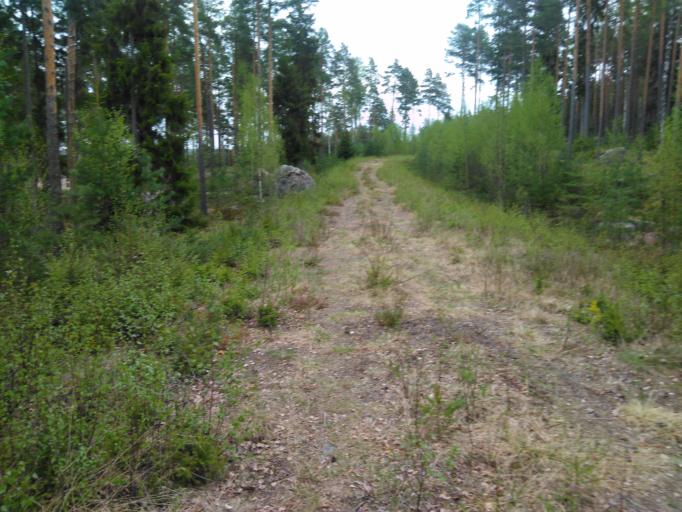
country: SE
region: Dalarna
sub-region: Faluns Kommun
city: Svardsjo
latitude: 60.6062
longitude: 15.8253
